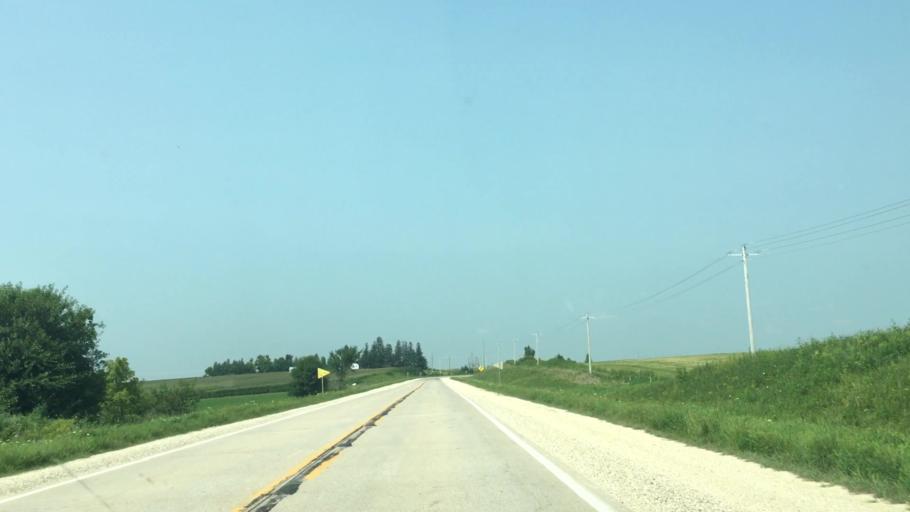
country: US
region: Iowa
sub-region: Fayette County
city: West Union
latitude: 43.1342
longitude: -91.8691
